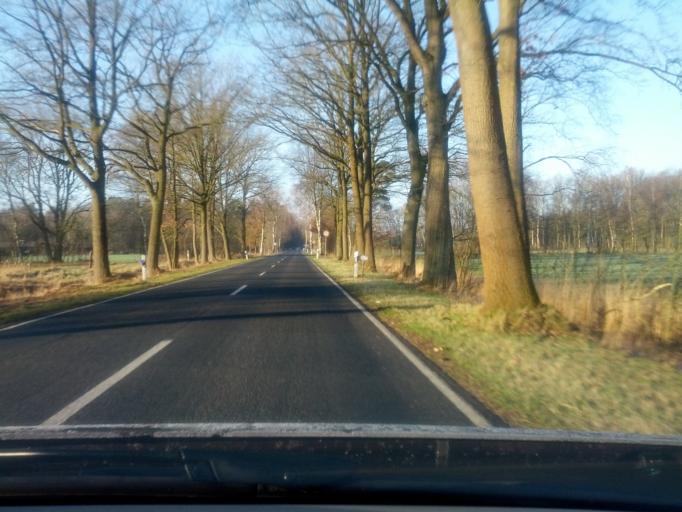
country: DE
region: Lower Saxony
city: Kalbe
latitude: 53.2797
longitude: 9.5709
